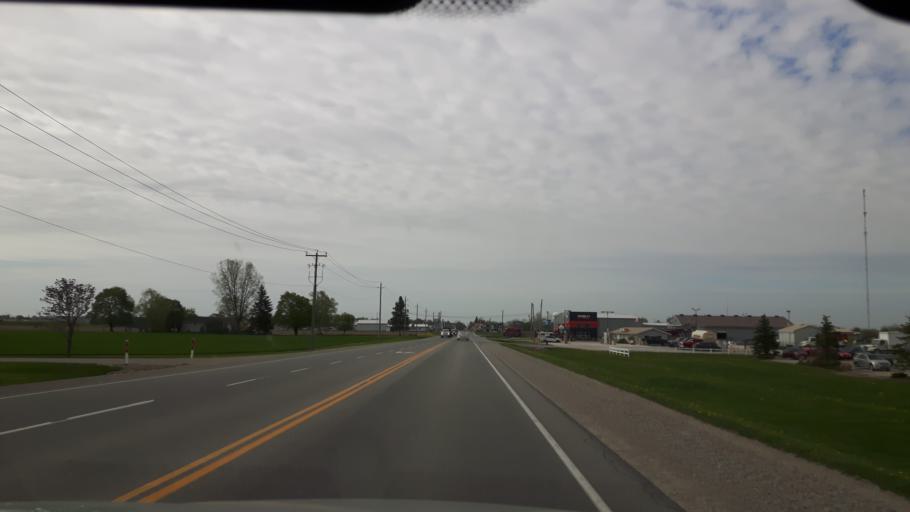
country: CA
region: Ontario
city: South Huron
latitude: 43.3682
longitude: -81.4849
